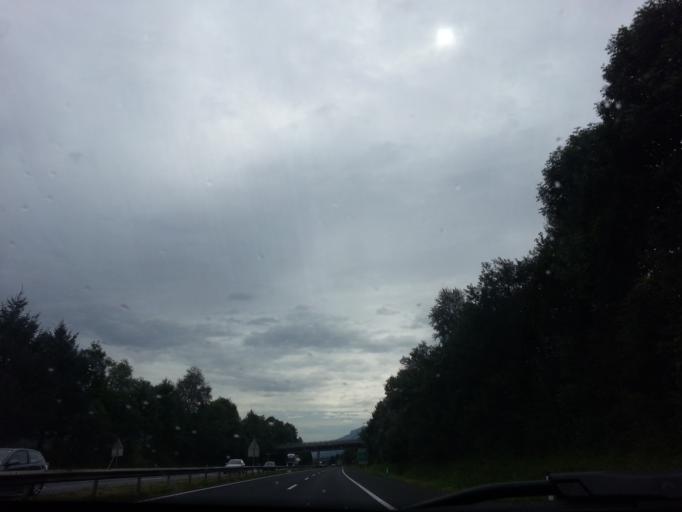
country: AT
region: Styria
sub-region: Politischer Bezirk Liezen
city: Rottenmann
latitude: 47.5130
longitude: 14.4185
